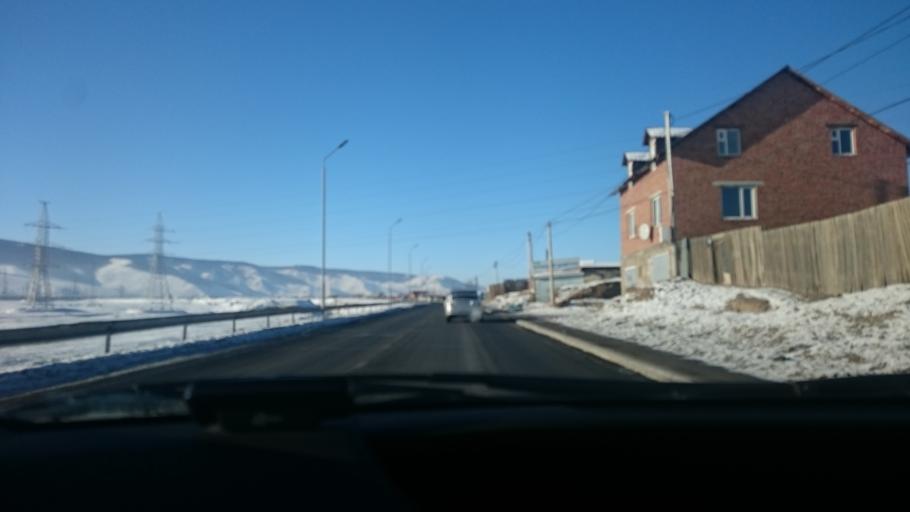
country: MN
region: Ulaanbaatar
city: Ulaanbaatar
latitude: 47.9137
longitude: 107.0490
